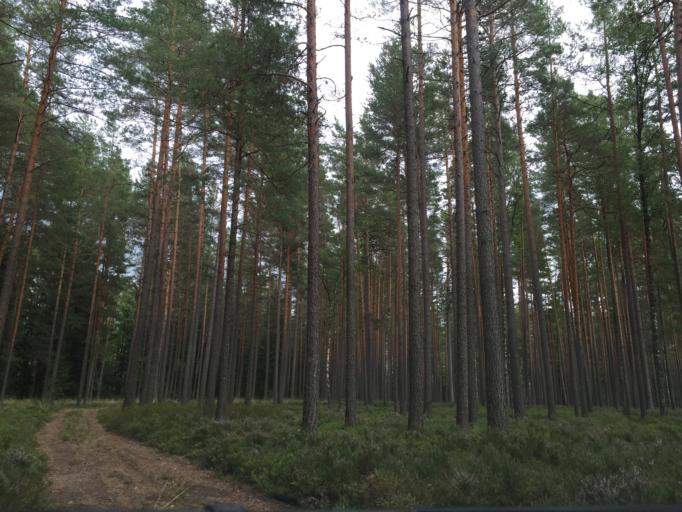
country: LV
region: Saulkrastu
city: Saulkrasti
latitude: 57.2140
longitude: 24.4473
